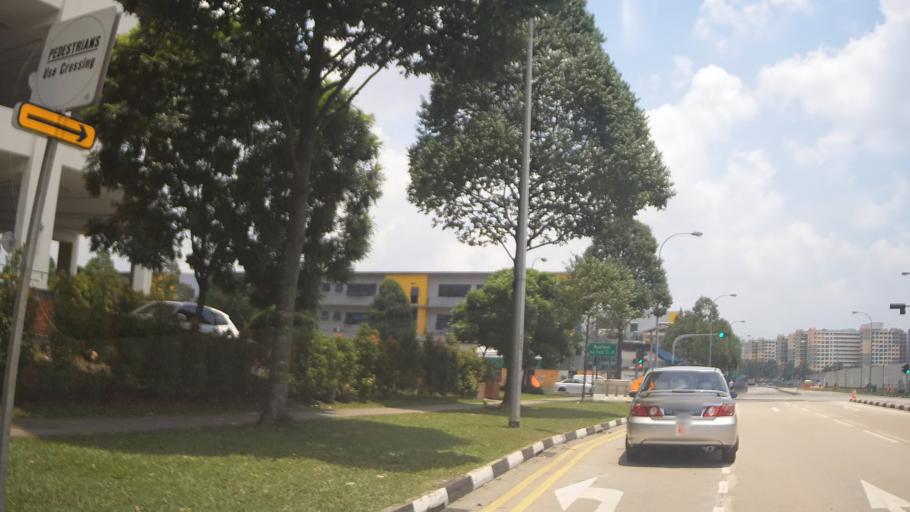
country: MY
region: Johor
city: Johor Bahru
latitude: 1.4501
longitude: 103.7906
